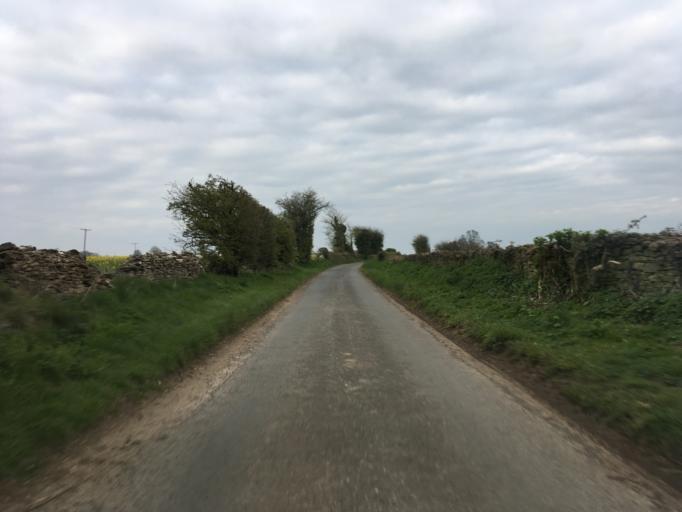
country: GB
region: England
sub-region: Wiltshire
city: Luckington
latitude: 51.6158
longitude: -2.2626
